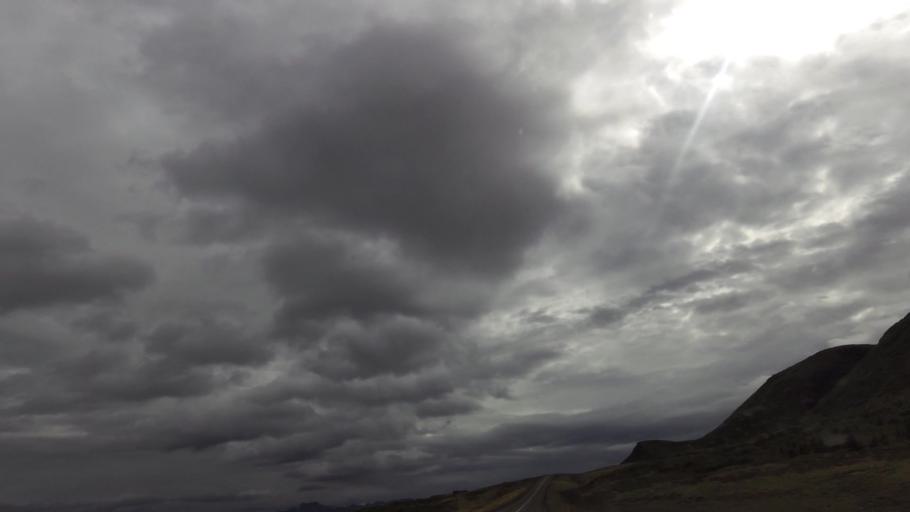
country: IS
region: West
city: Stykkisholmur
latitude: 65.5095
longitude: -22.1117
